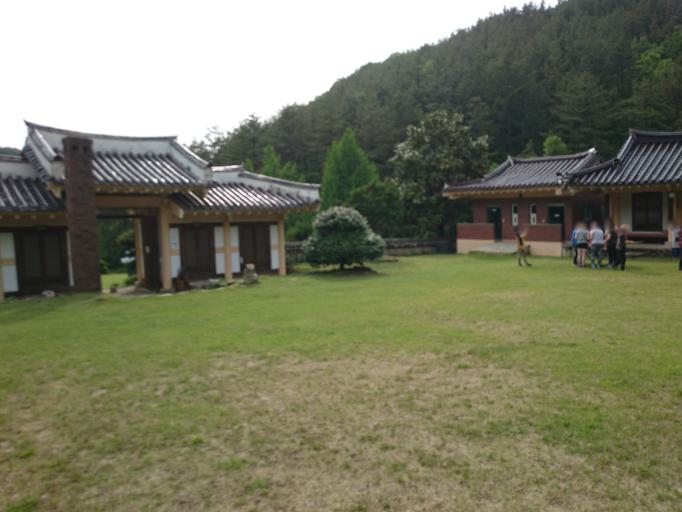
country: KR
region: Jeollabuk-do
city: Wanju
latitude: 35.9057
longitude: 127.2093
